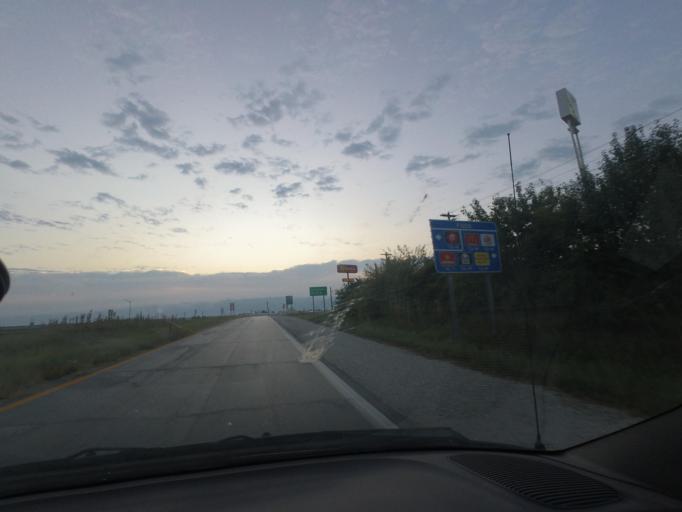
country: US
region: Missouri
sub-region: Macon County
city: Macon
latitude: 39.7535
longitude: -92.4692
